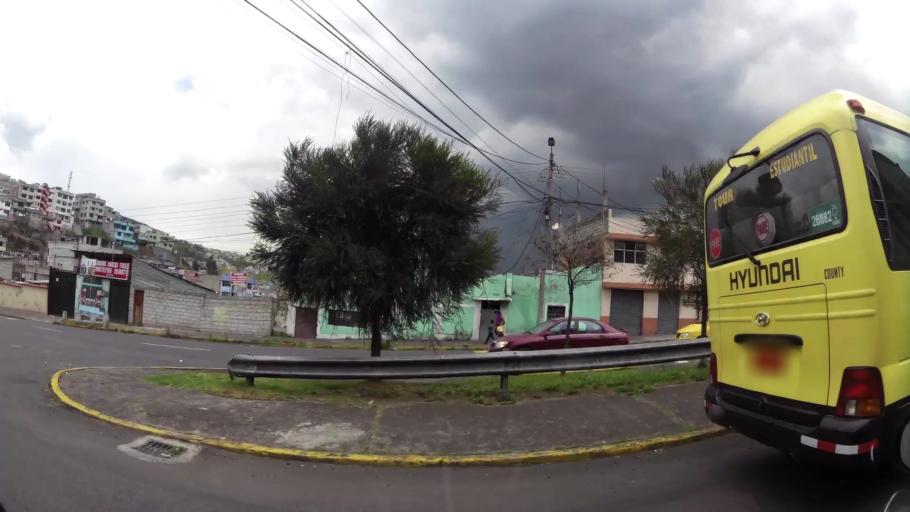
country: EC
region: Pichincha
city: Quito
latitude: -0.2500
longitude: -78.5129
